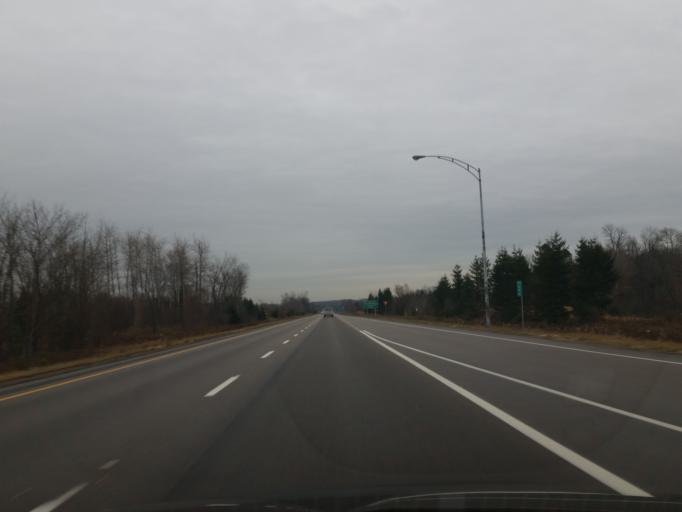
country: CA
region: Quebec
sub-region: Capitale-Nationale
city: Saint-Augustin-de-Desmaures
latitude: 46.7476
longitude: -71.5163
